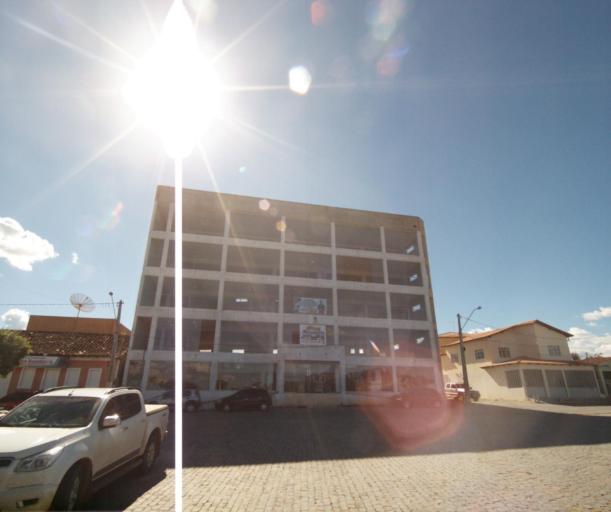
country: BR
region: Bahia
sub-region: Carinhanha
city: Carinhanha
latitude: -14.1783
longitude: -44.5320
